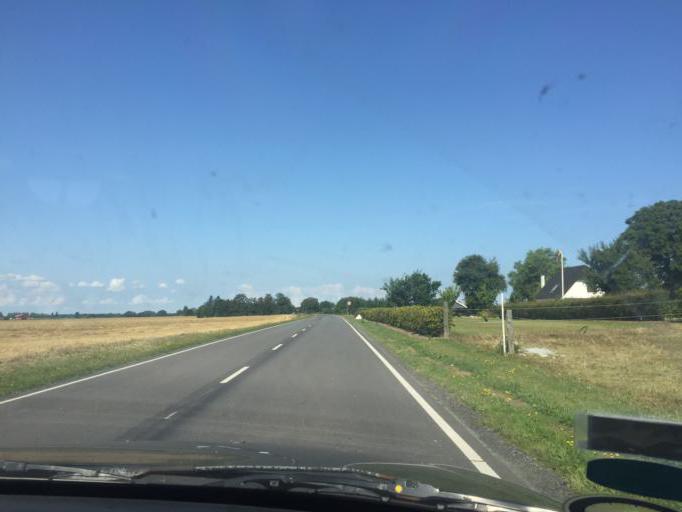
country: DK
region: Zealand
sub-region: Guldborgsund Kommune
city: Sakskobing
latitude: 54.7941
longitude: 11.5679
